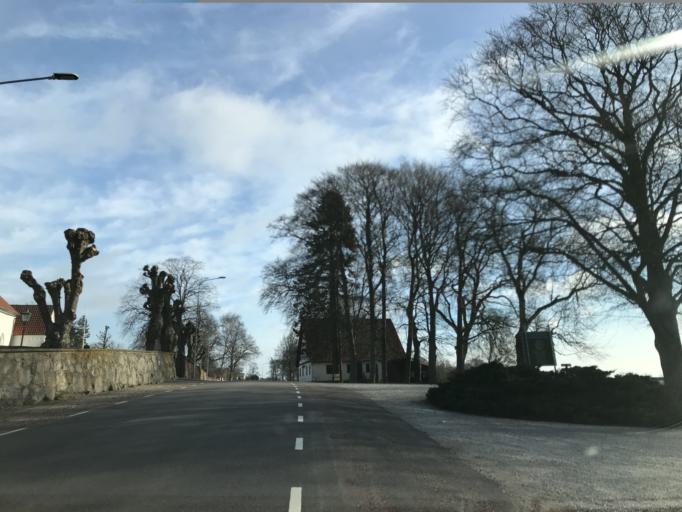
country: SE
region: Skane
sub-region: Hoors Kommun
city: Loberod
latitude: 55.7241
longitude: 13.5264
